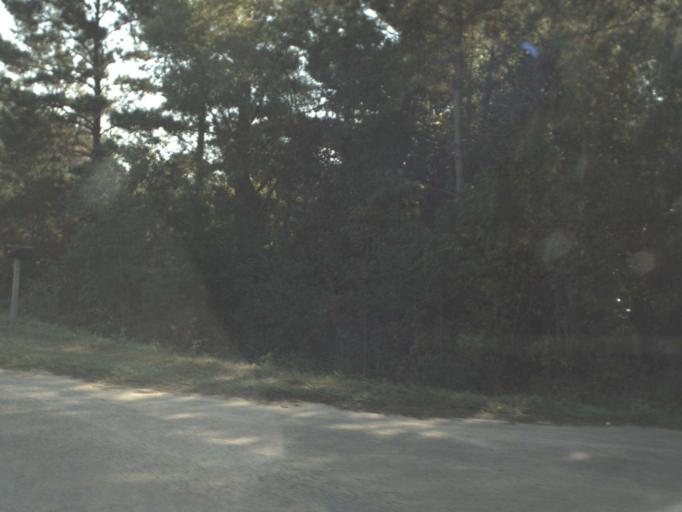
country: US
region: Florida
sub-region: Holmes County
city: Bonifay
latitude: 30.6096
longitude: -85.7154
